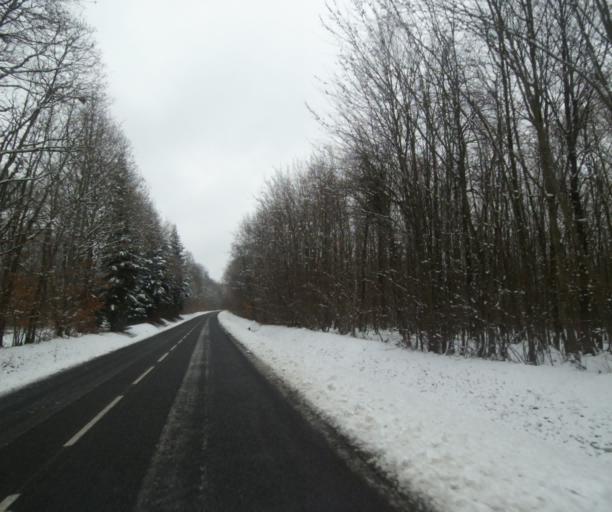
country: FR
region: Champagne-Ardenne
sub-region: Departement de la Haute-Marne
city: Laneuville-a-Remy
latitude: 48.4469
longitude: 4.8636
